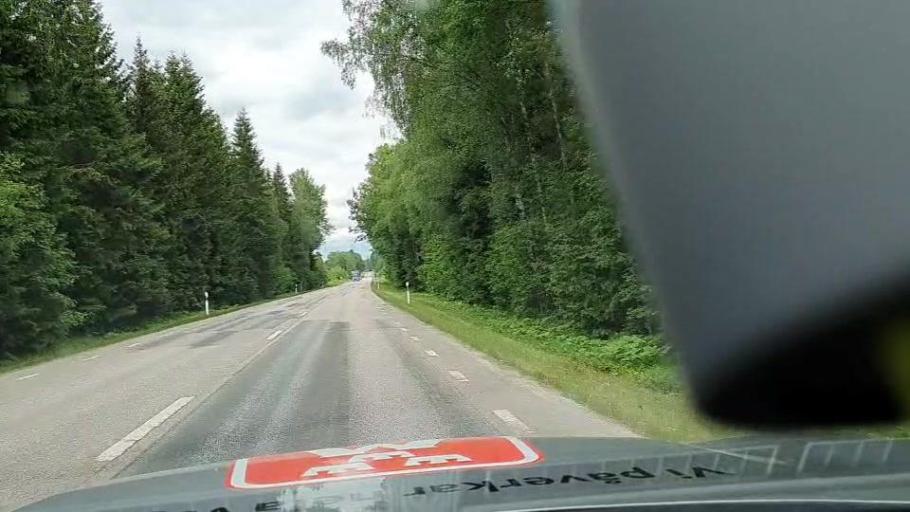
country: SE
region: Kalmar
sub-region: Emmaboda Kommun
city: Emmaboda
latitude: 56.5101
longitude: 15.6060
